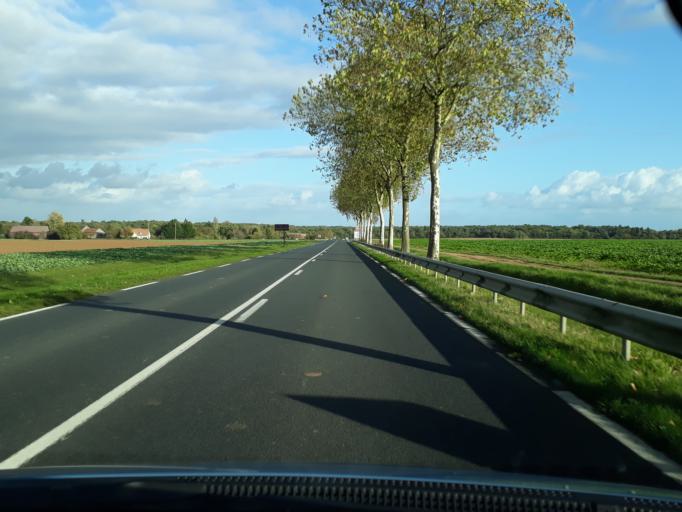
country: FR
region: Ile-de-France
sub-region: Departement de Seine-et-Marne
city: Noisy-sur-Ecole
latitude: 48.3053
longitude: 2.5013
